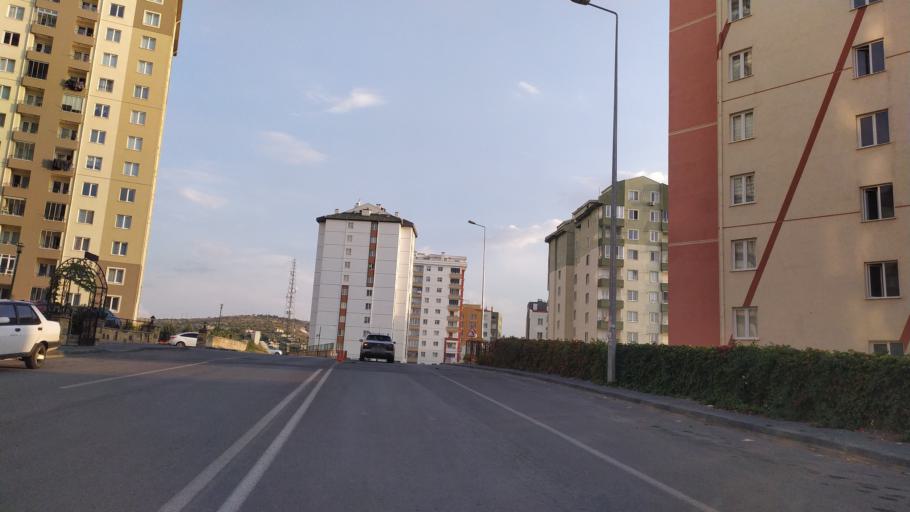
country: TR
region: Kayseri
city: Talas
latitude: 38.7006
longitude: 35.5640
